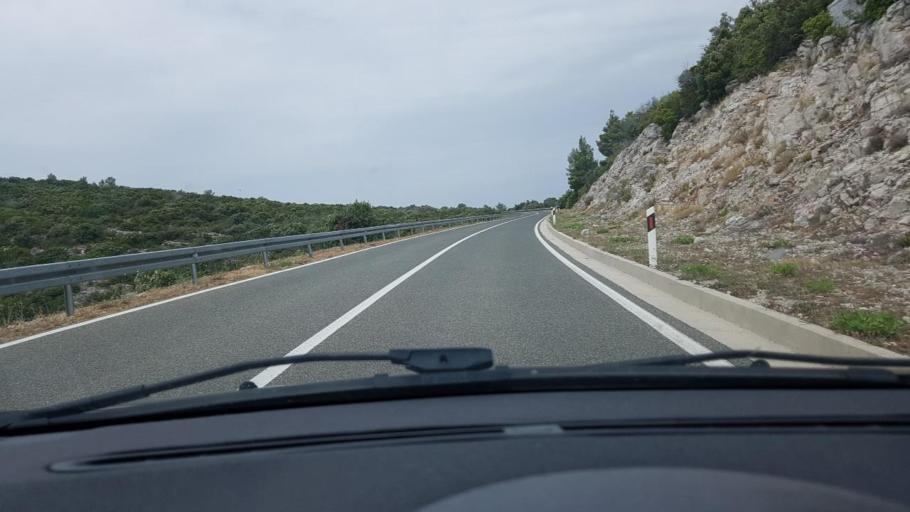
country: HR
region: Dubrovacko-Neretvanska
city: Smokvica
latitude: 42.9461
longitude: 16.9534
